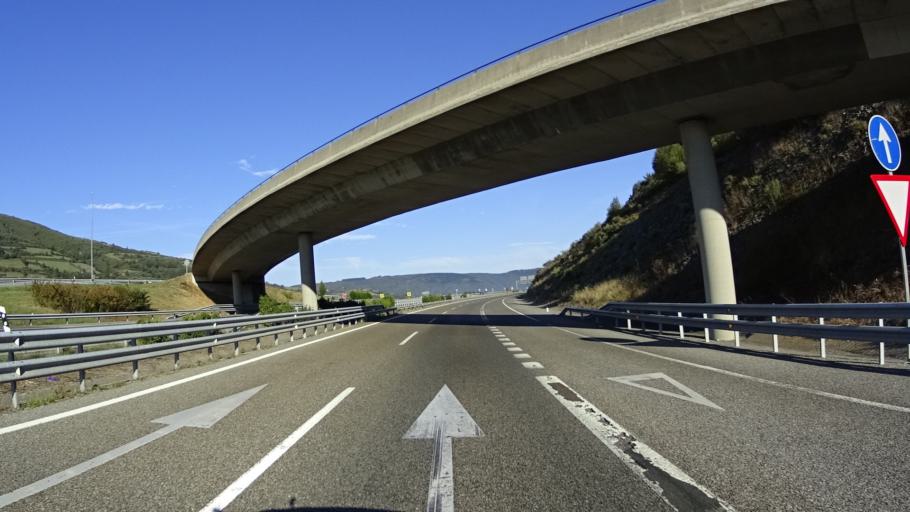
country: ES
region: Galicia
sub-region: Provincia de Lugo
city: San Roman
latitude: 42.7645
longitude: -7.0833
